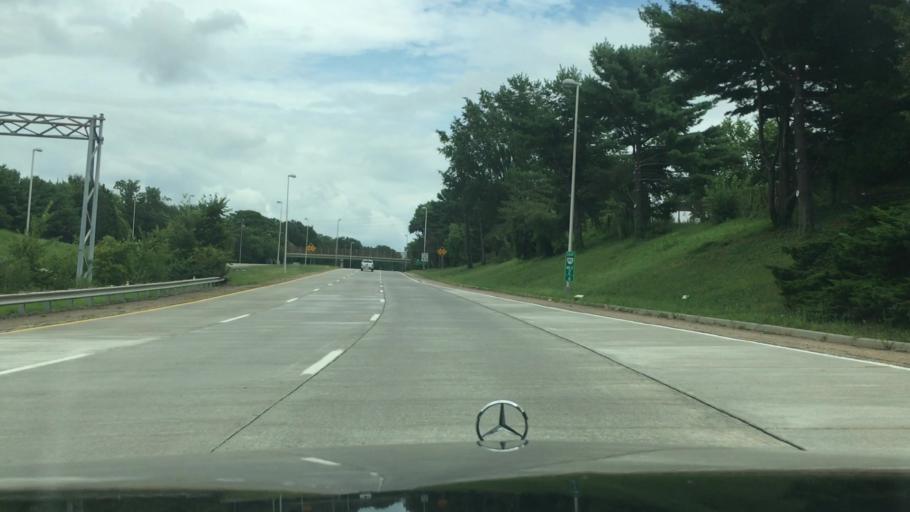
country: US
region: Virginia
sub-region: City of Richmond
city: Richmond
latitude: 37.5478
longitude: -77.4745
